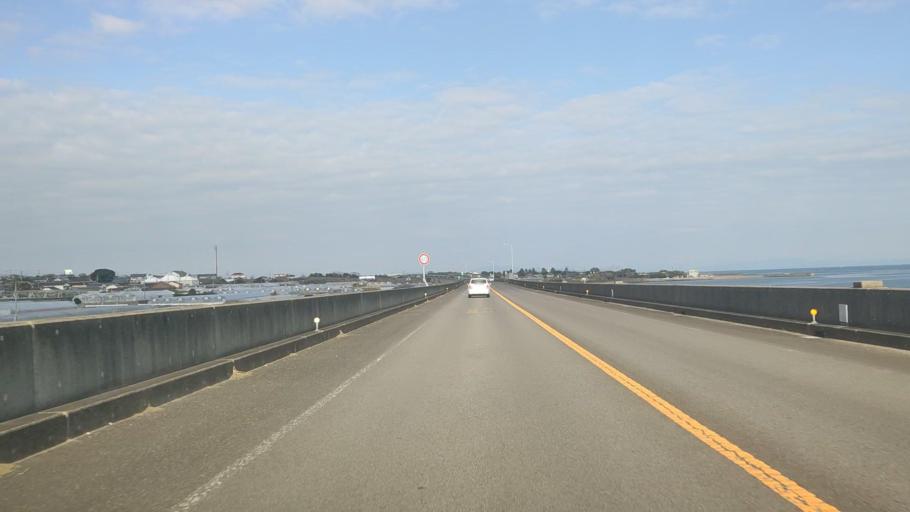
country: JP
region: Nagasaki
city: Shimabara
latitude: 32.7309
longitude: 130.3668
